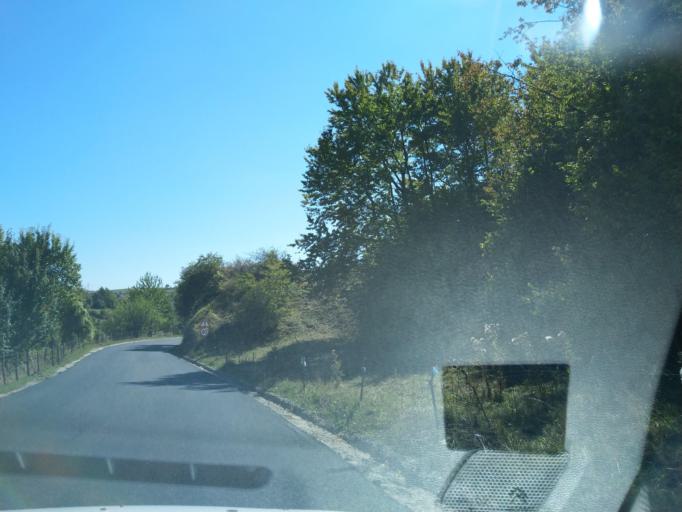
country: RS
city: Sokolovica
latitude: 43.2564
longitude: 20.2296
